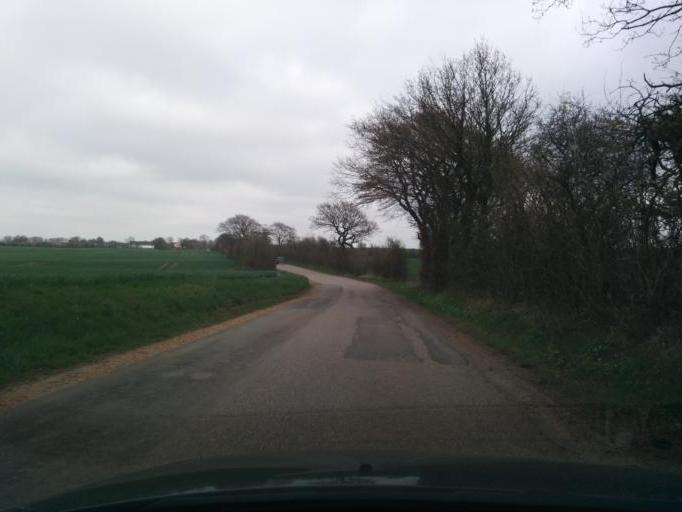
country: DK
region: South Denmark
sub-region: Kolding Kommune
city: Christiansfeld
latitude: 55.3909
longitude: 9.3968
